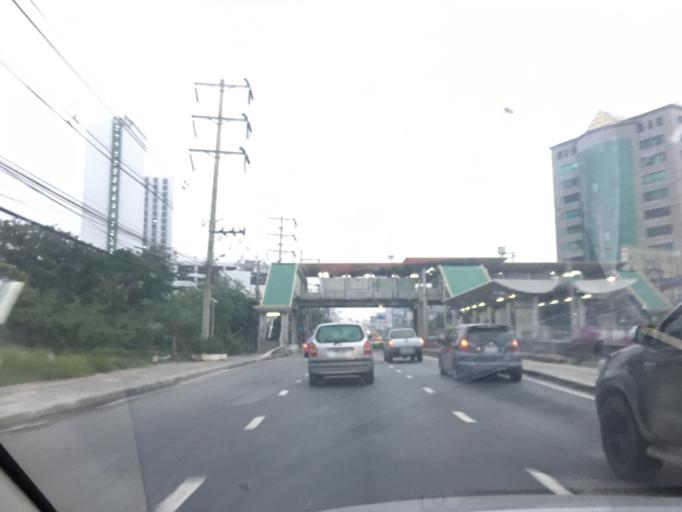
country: TH
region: Bangkok
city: Bang Kho Laem
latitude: 13.6933
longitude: 100.5005
